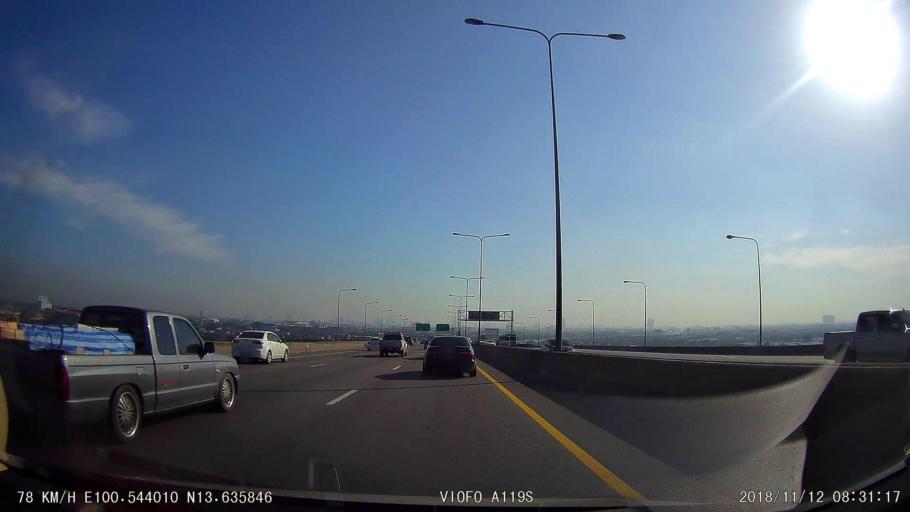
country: TH
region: Samut Prakan
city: Phra Pradaeng
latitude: 13.6359
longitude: 100.5442
